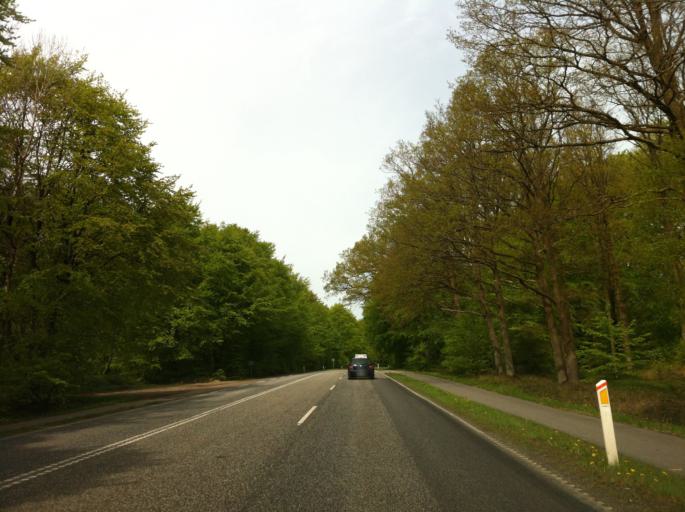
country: DK
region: Capital Region
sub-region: Allerod Kommune
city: Lillerod
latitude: 55.9020
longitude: 12.3578
